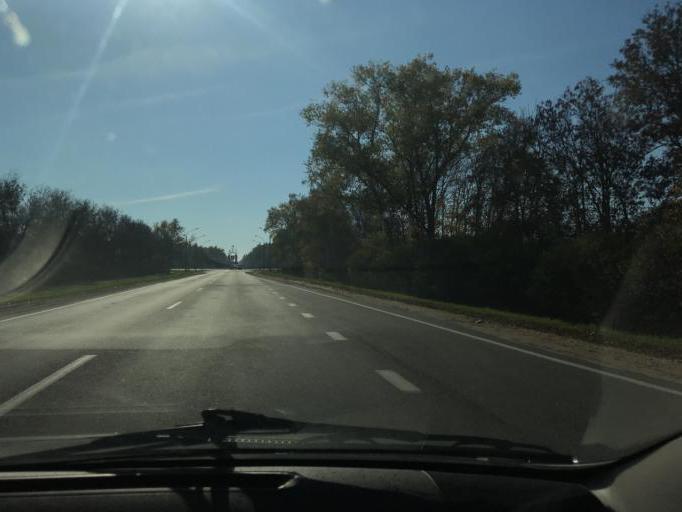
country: BY
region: Minsk
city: Starobin
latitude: 52.7848
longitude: 27.4646
